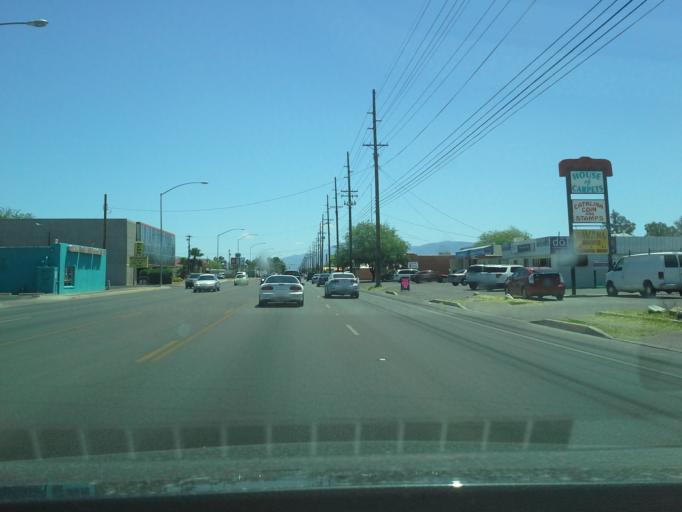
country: US
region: Arizona
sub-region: Pima County
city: Tucson
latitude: 32.2506
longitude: -110.9071
